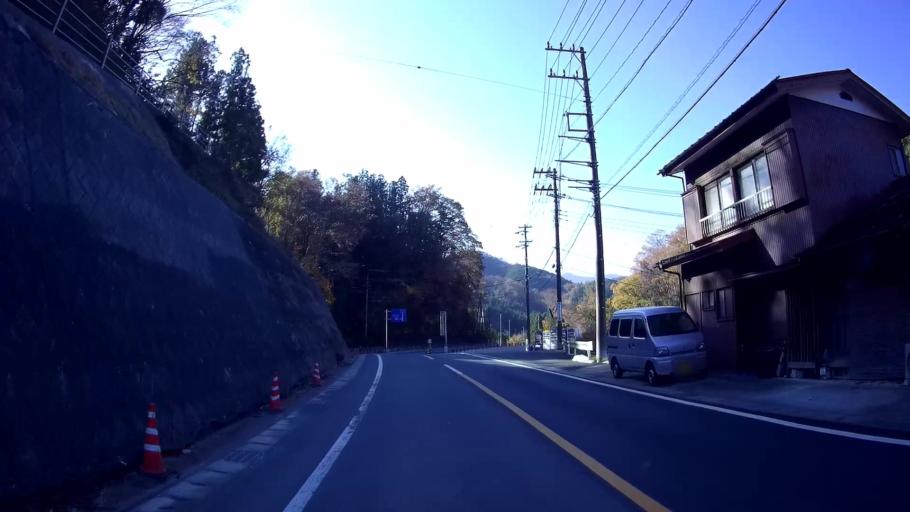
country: JP
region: Yamanashi
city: Uenohara
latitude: 35.5960
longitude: 139.1210
